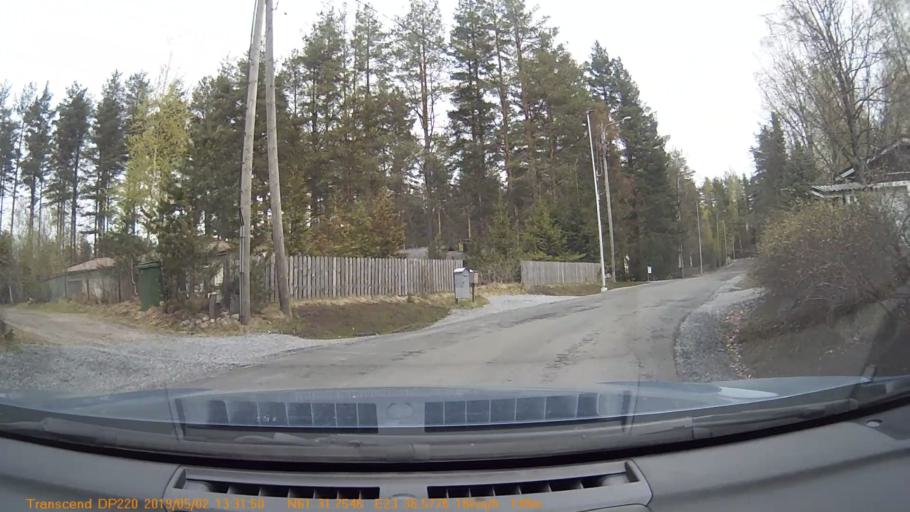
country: FI
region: Pirkanmaa
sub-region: Tampere
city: Yloejaervi
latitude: 61.5292
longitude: 23.6096
